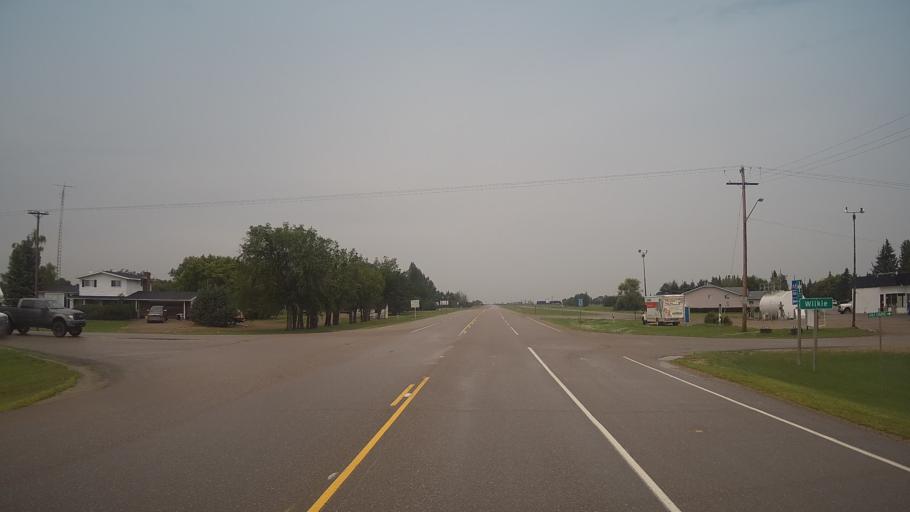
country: CA
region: Saskatchewan
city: Wilkie
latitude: 52.4050
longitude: -108.7140
